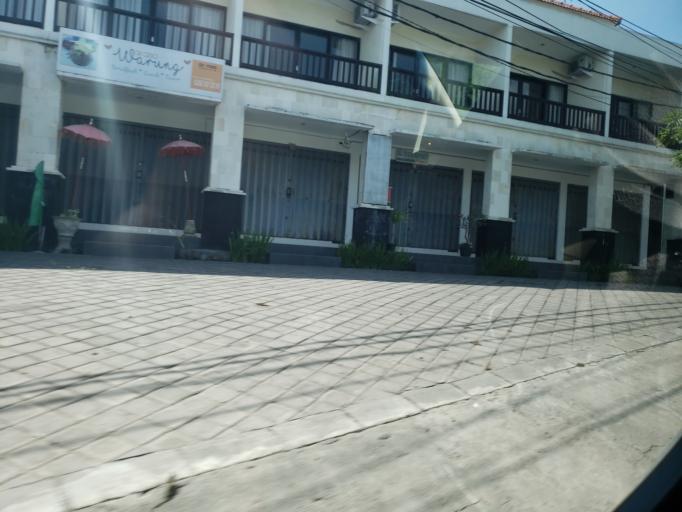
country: ID
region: Bali
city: Kangin
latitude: -8.8291
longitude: 115.1496
